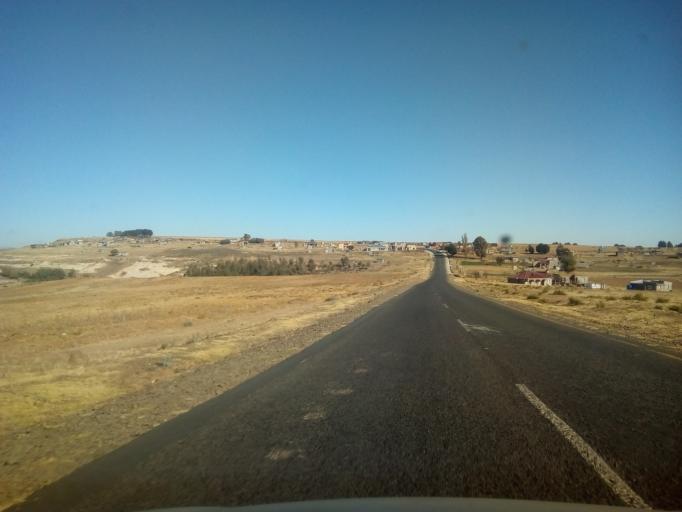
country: LS
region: Maseru
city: Maseru
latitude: -29.2930
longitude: 27.6248
